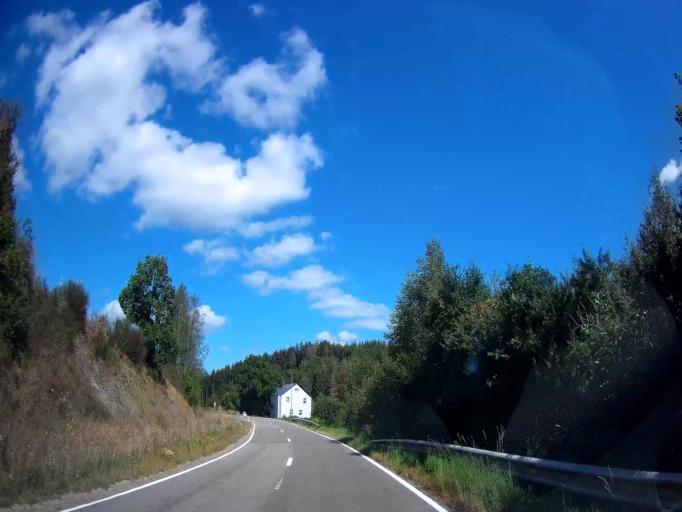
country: BE
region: Wallonia
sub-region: Province du Luxembourg
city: Bertogne
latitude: 50.0917
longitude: 5.6740
